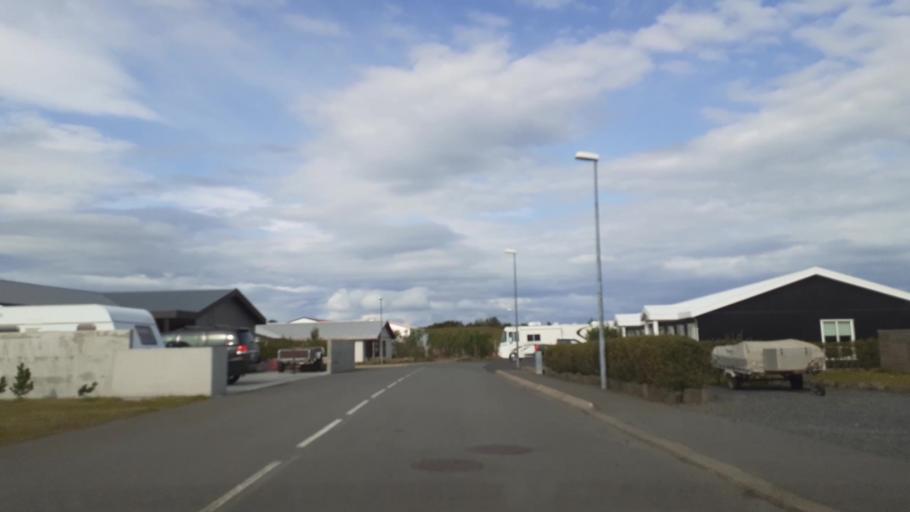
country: IS
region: South
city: Vestmannaeyjar
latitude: 63.8343
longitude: -20.3878
